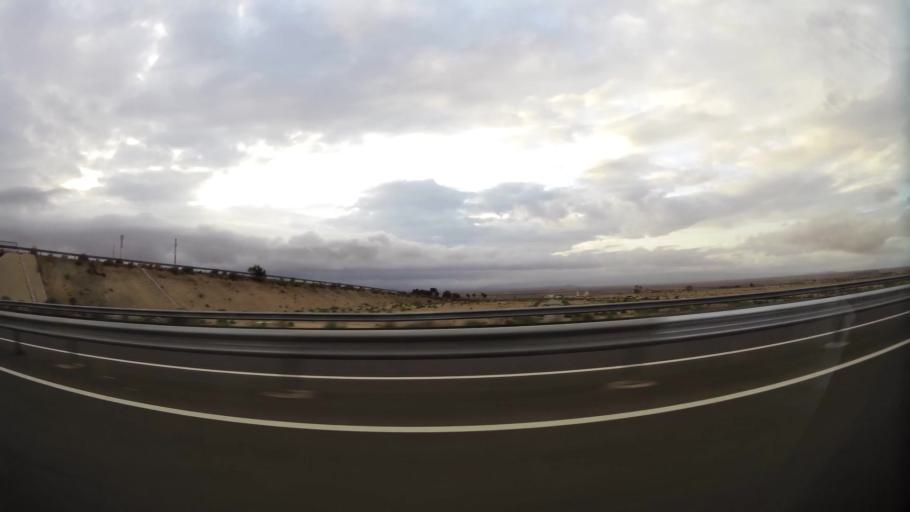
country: MA
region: Taza-Al Hoceima-Taounate
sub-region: Taza
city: Guercif
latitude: 34.4078
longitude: -3.1714
